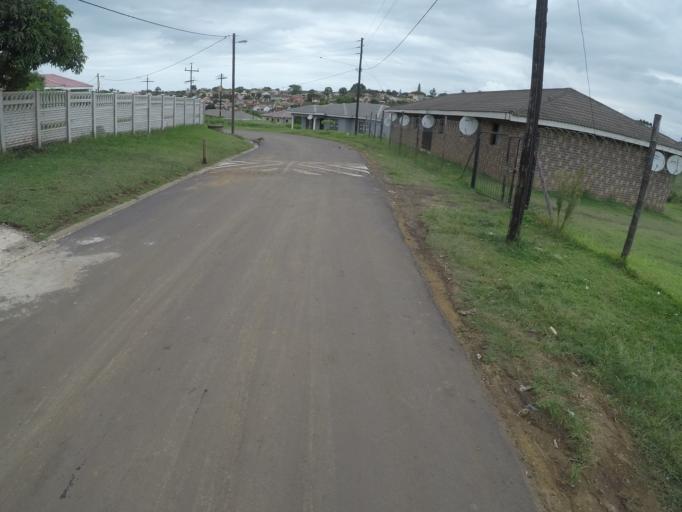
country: ZA
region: KwaZulu-Natal
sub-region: uThungulu District Municipality
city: Empangeni
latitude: -28.7735
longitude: 31.8532
